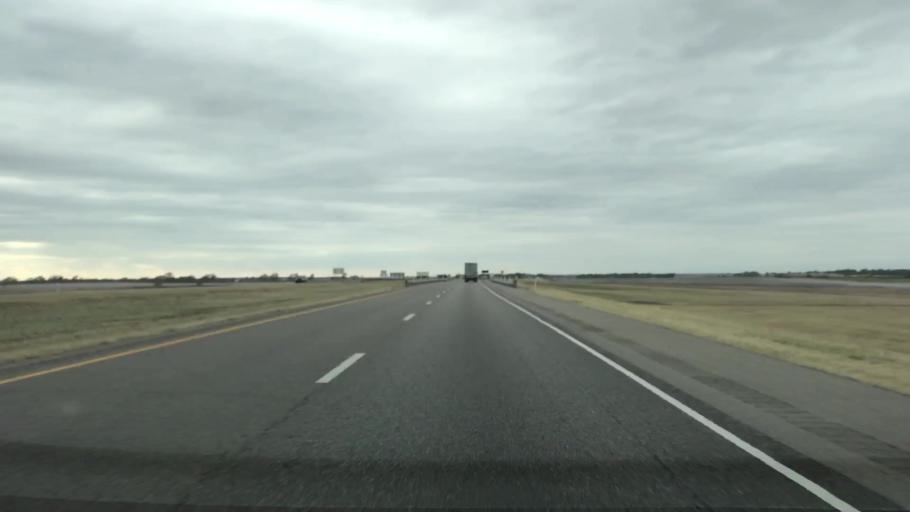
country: US
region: Oklahoma
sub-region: Beckham County
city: Erick
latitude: 35.2282
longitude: -99.9889
